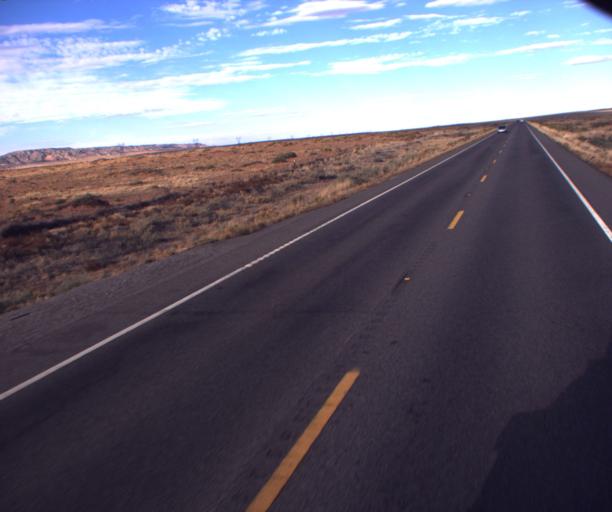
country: US
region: Arizona
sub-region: Apache County
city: Lukachukai
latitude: 36.9451
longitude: -109.2655
